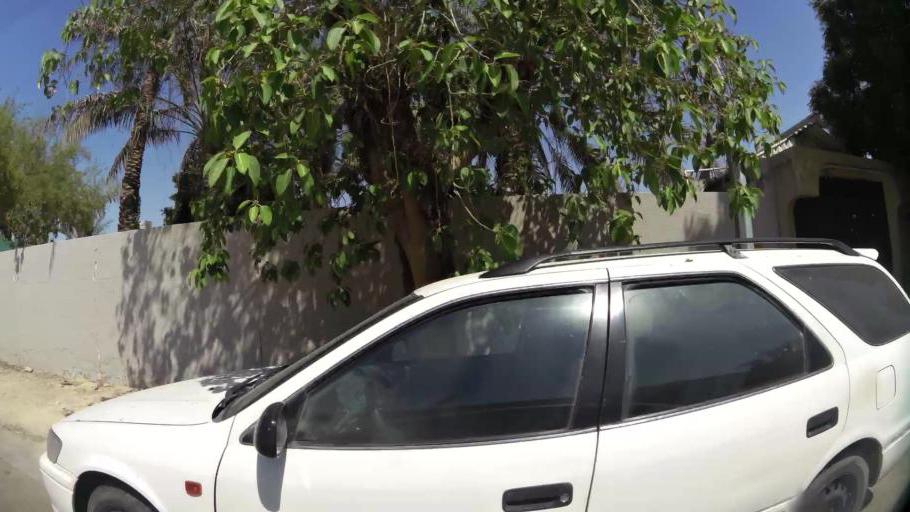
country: AE
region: Ash Shariqah
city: Sharjah
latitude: 25.2688
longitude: 55.3675
